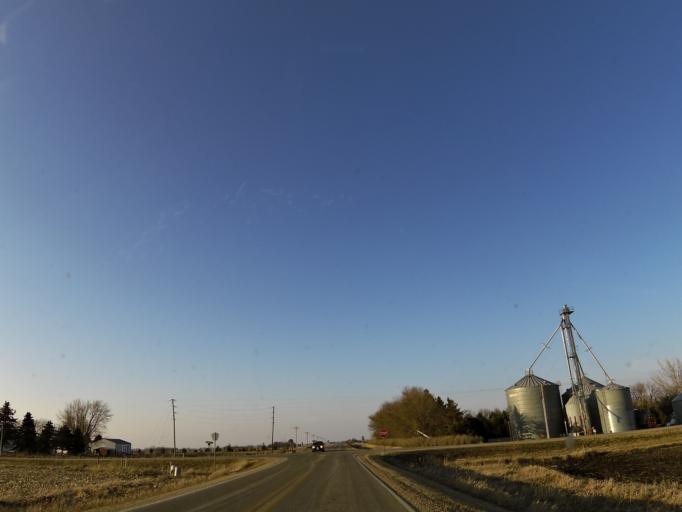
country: US
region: Iowa
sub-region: Worth County
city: Northwood
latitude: 43.4396
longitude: -93.1244
